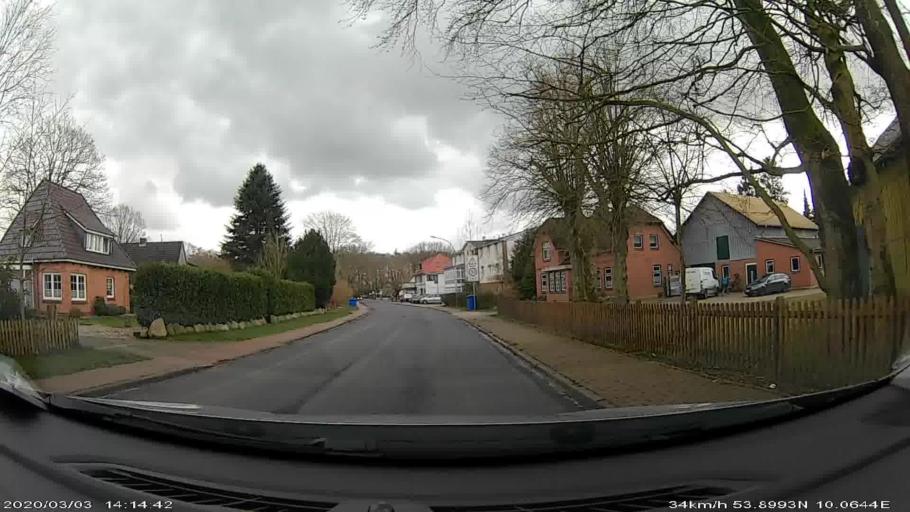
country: DE
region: Schleswig-Holstein
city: Hartenholm
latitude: 53.8991
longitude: 10.0649
